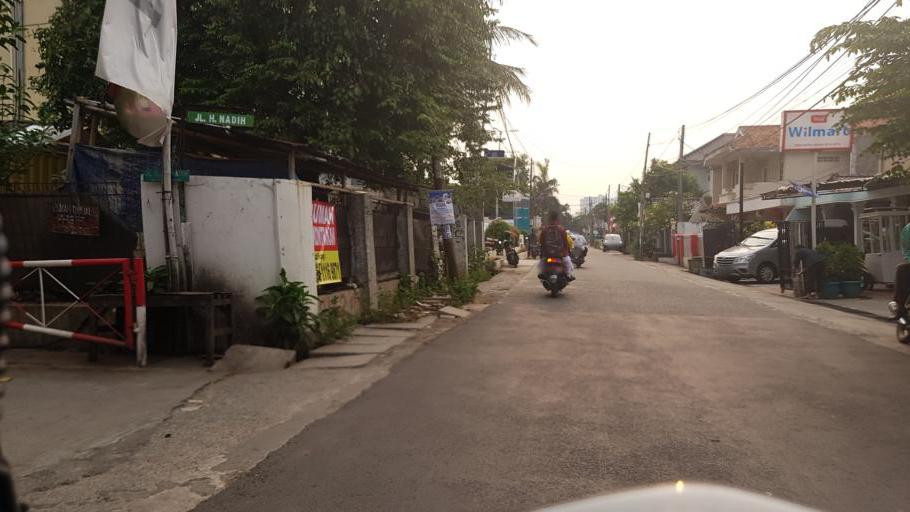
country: ID
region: West Java
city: Depok
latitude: -6.3726
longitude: 106.8445
